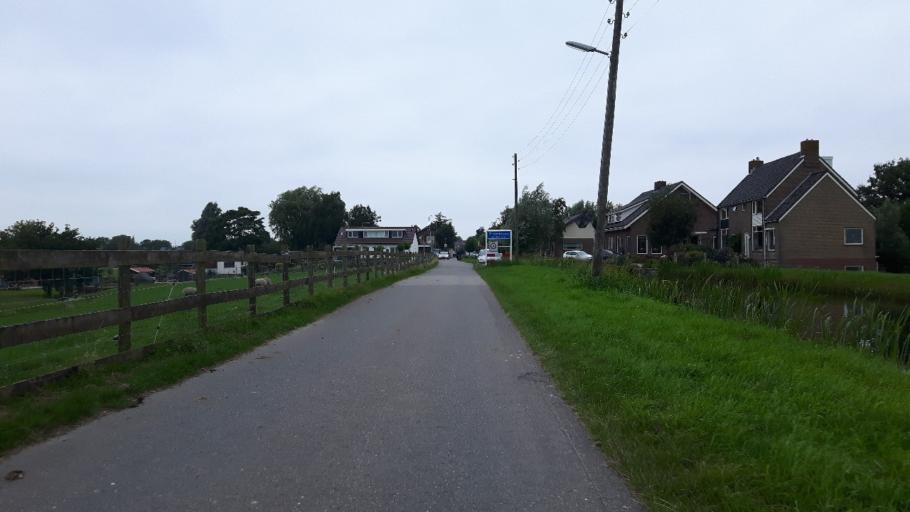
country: NL
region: South Holland
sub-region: Gemeente Nieuwkoop
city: Nieuwkoop
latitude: 52.1777
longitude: 4.7866
